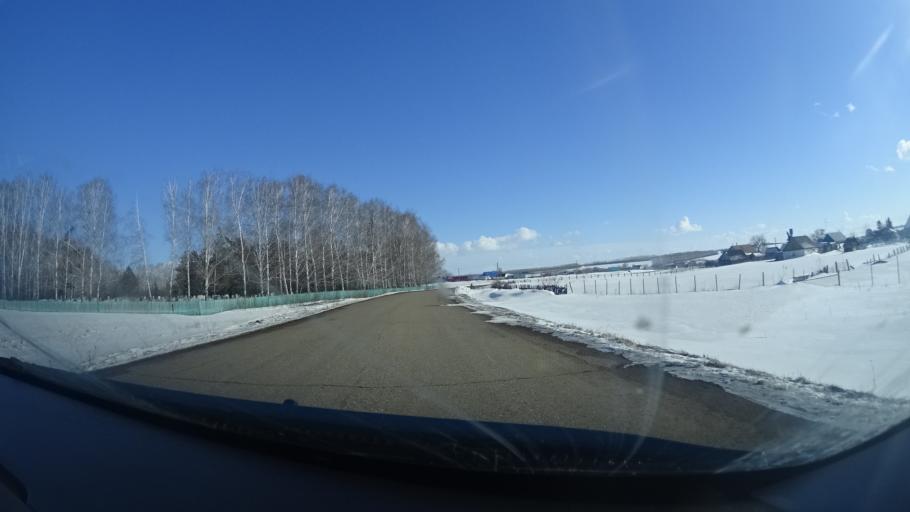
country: RU
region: Bashkortostan
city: Chishmy
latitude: 54.5980
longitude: 55.2562
